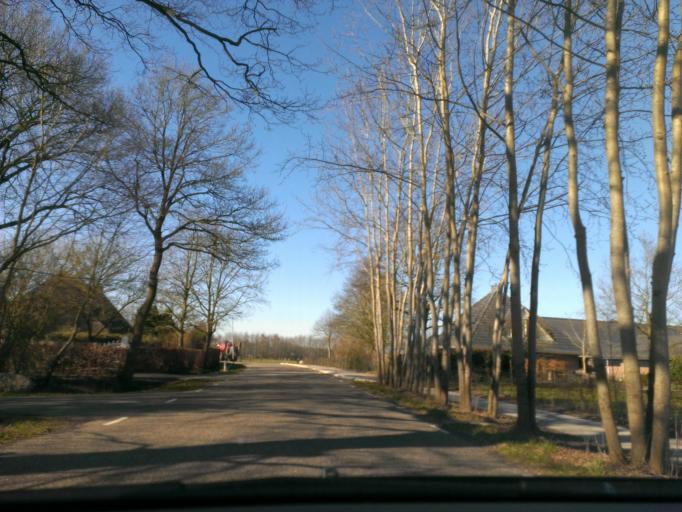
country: NL
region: Drenthe
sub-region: Gemeente De Wolden
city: Ruinen
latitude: 52.6885
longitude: 6.3494
